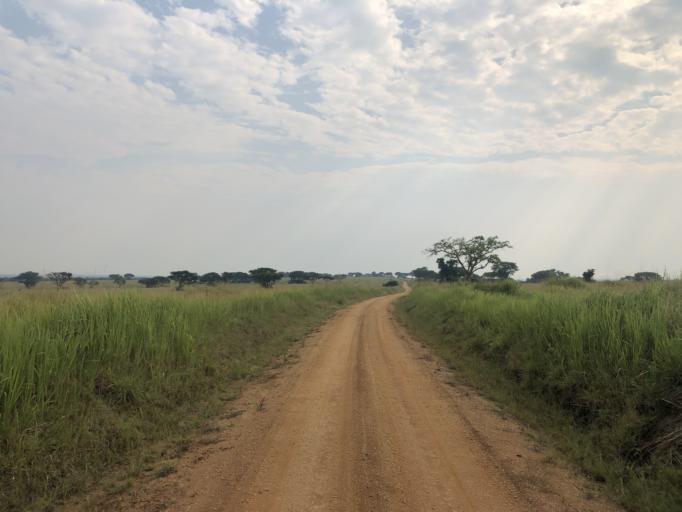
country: UG
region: Western Region
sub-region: Mitoma District
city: Mitoma
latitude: -0.5202
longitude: 29.7988
